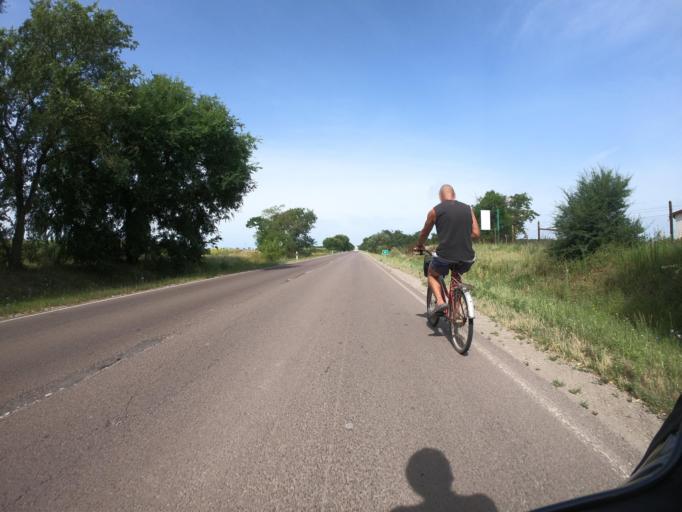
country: HU
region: Jasz-Nagykun-Szolnok
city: Tiszafured
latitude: 47.6027
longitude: 20.7906
